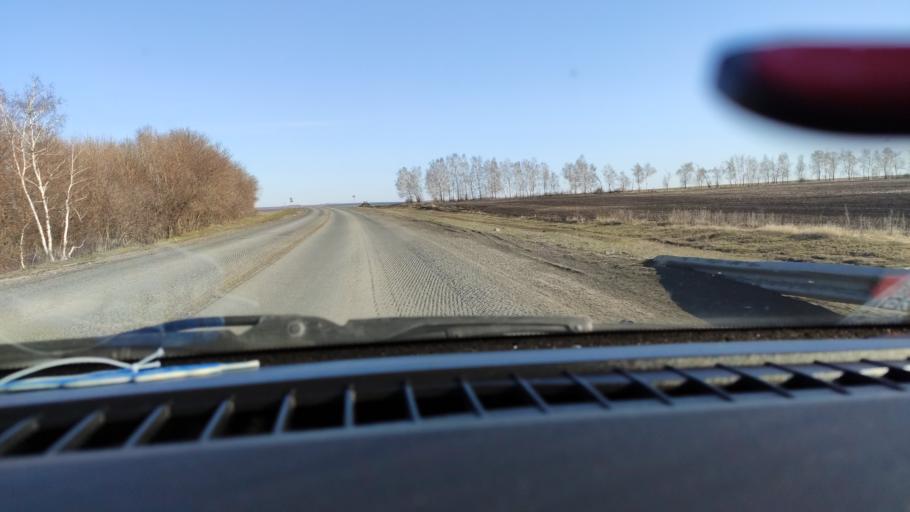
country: RU
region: Saratov
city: Dukhovnitskoye
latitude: 52.7181
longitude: 48.2658
